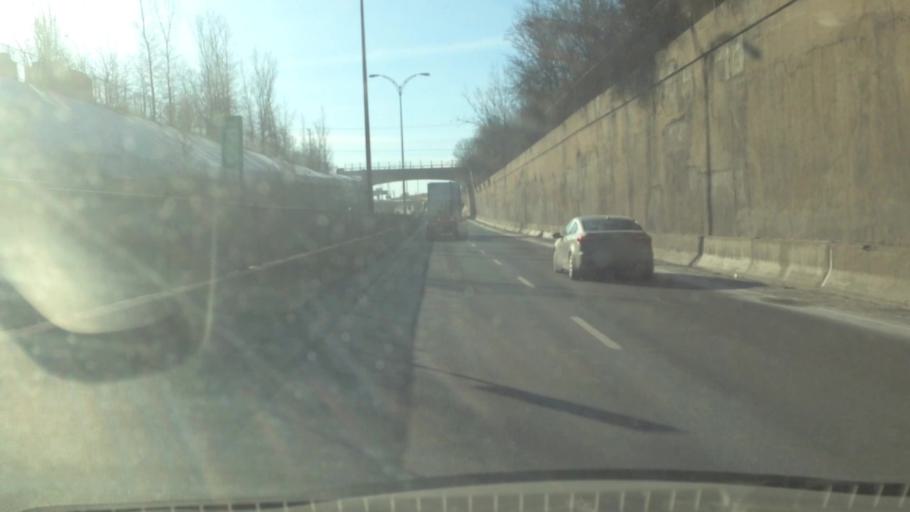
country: CA
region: Quebec
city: Montreal-Ouest
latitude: 45.4271
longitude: -73.6502
